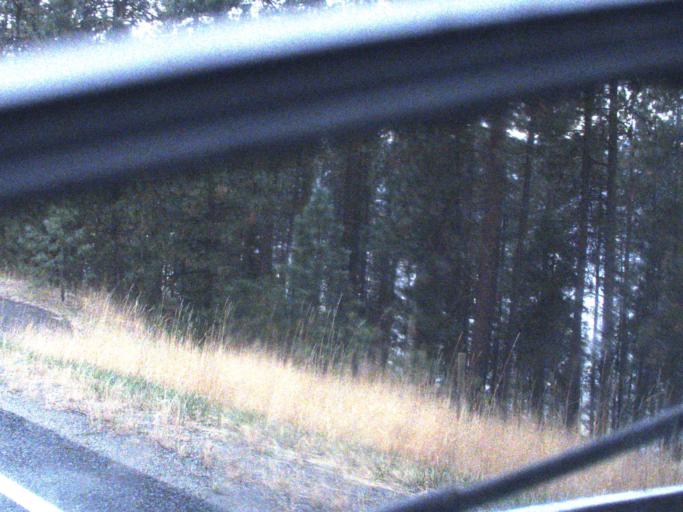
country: US
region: Washington
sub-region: Stevens County
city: Kettle Falls
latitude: 48.4985
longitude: -118.1595
